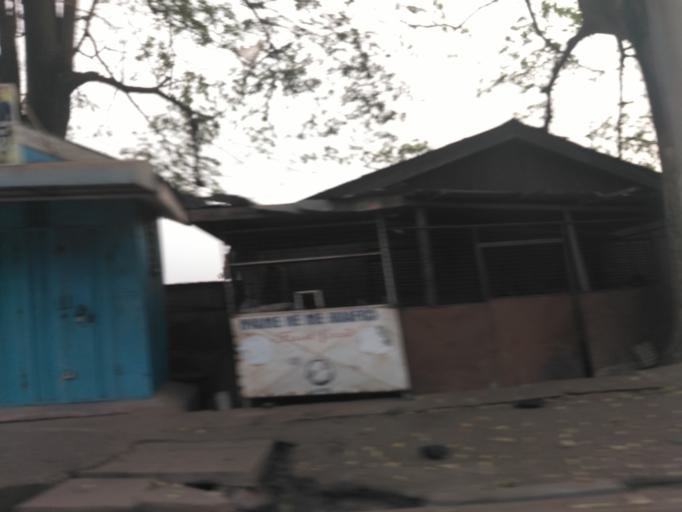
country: GH
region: Ashanti
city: Kumasi
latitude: 6.6849
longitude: -1.6171
